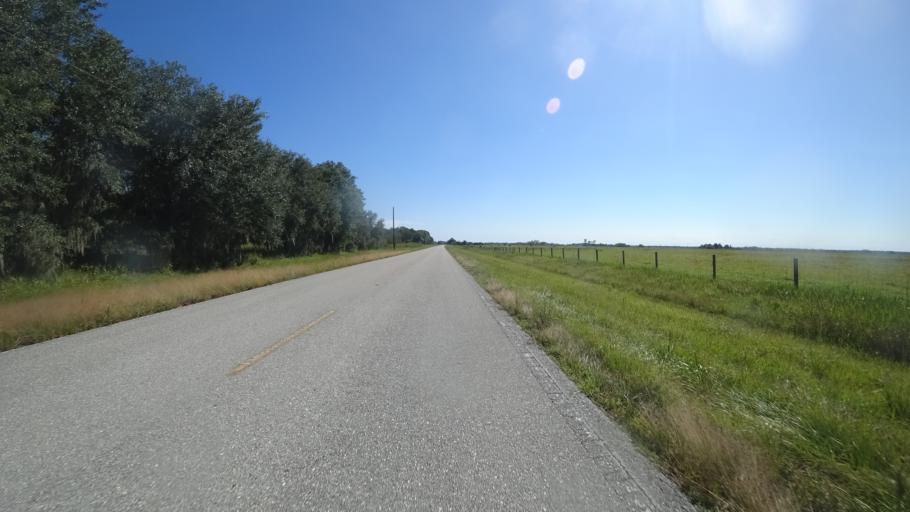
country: US
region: Florida
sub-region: DeSoto County
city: Nocatee
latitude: 27.2709
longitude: -82.0991
